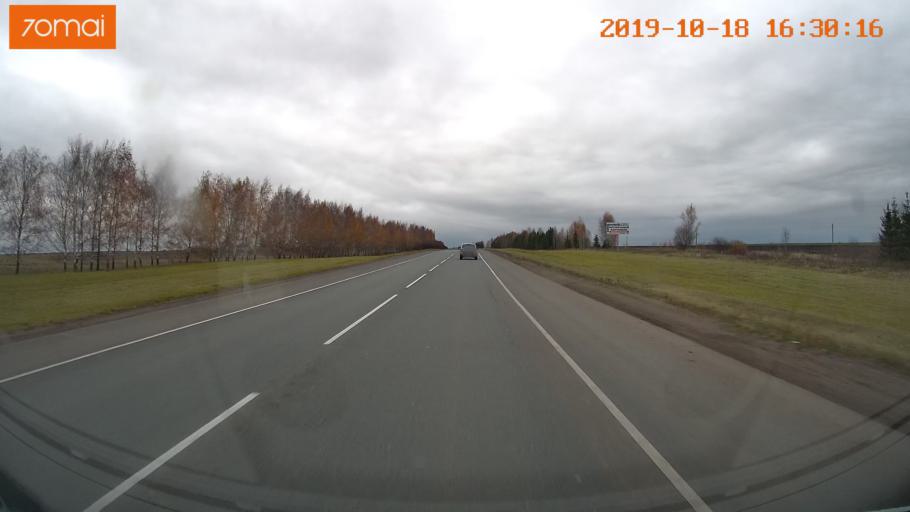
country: RU
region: Vladimir
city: Suzdal'
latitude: 56.3346
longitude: 40.4734
